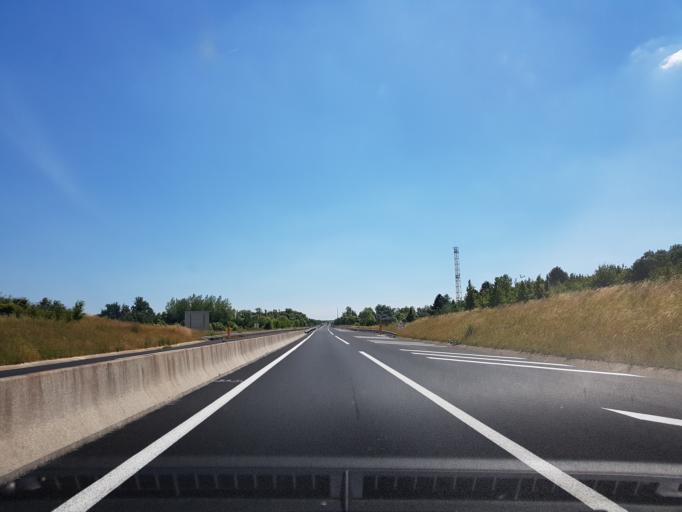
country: FR
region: Picardie
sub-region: Departement de la Somme
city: Nesle
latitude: 49.8350
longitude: 2.9214
